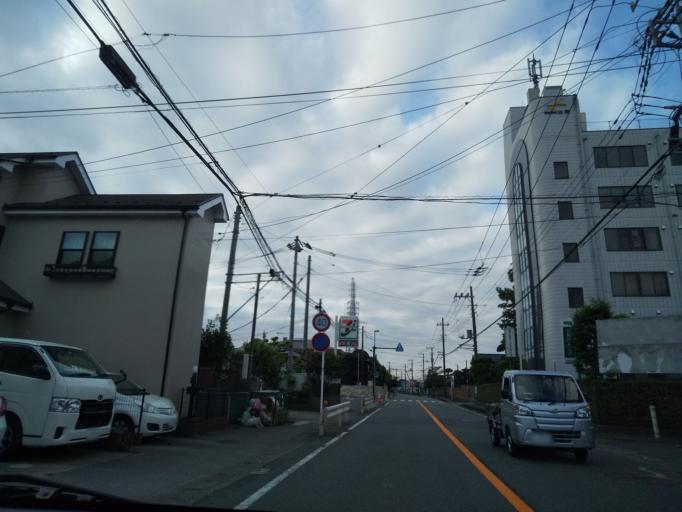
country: JP
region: Kanagawa
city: Zama
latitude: 35.5377
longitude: 139.3688
